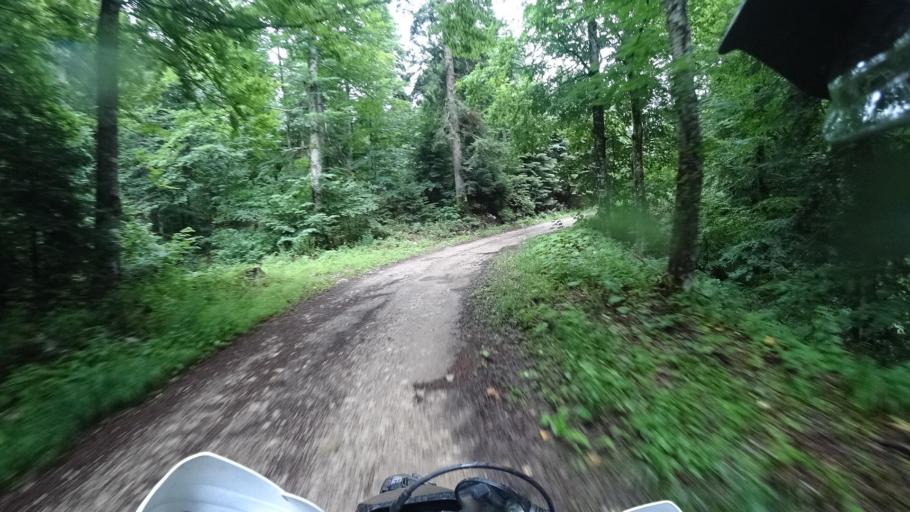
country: HR
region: Karlovacka
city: Plaski
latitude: 44.9282
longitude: 15.4296
